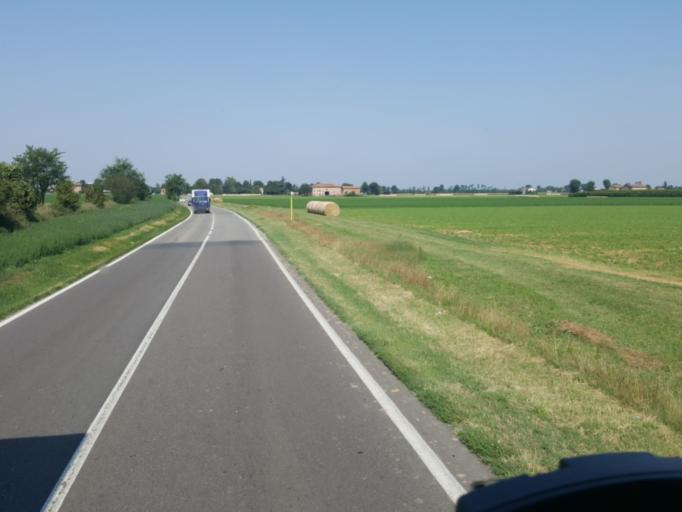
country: IT
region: Emilia-Romagna
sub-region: Provincia di Modena
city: San Vito
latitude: 44.5359
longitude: 10.9785
